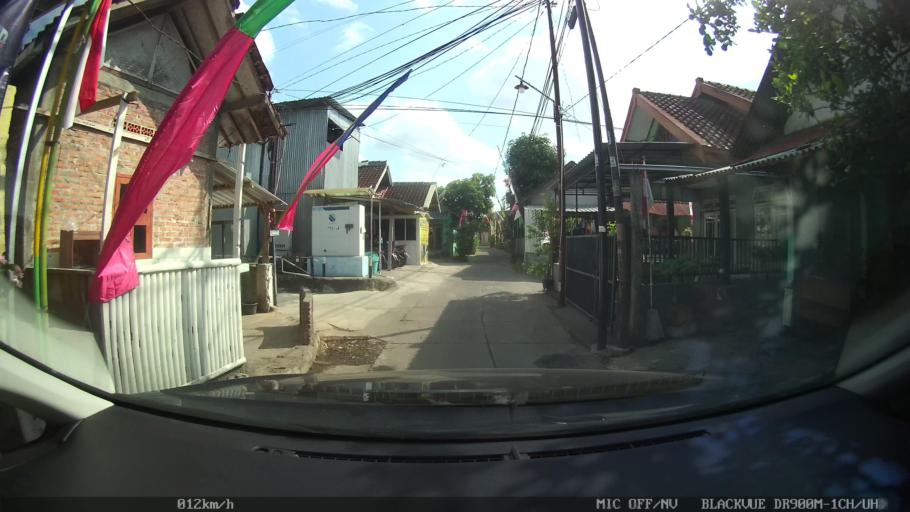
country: ID
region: Daerah Istimewa Yogyakarta
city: Kasihan
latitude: -7.8319
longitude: 110.3647
